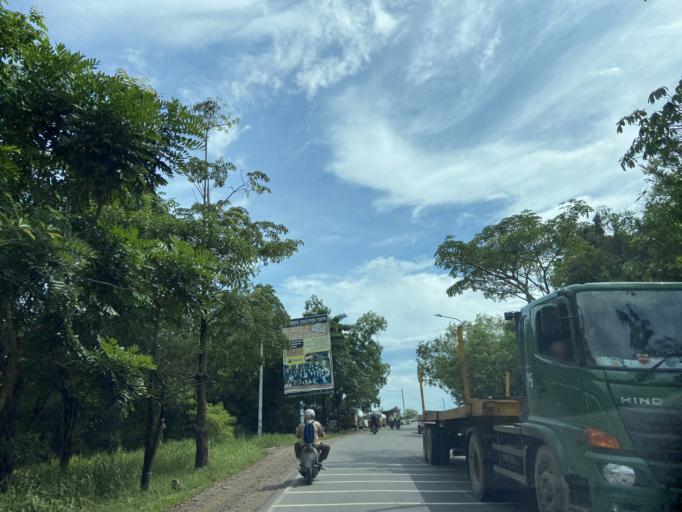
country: SG
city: Singapore
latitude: 1.0540
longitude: 103.9573
